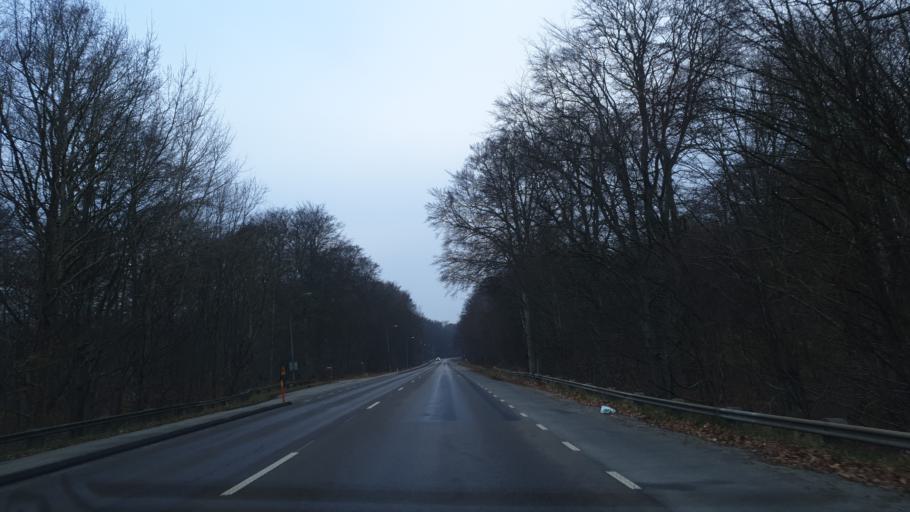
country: SE
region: Blekinge
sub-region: Solvesborgs Kommun
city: Soelvesborg
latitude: 56.0563
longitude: 14.5614
